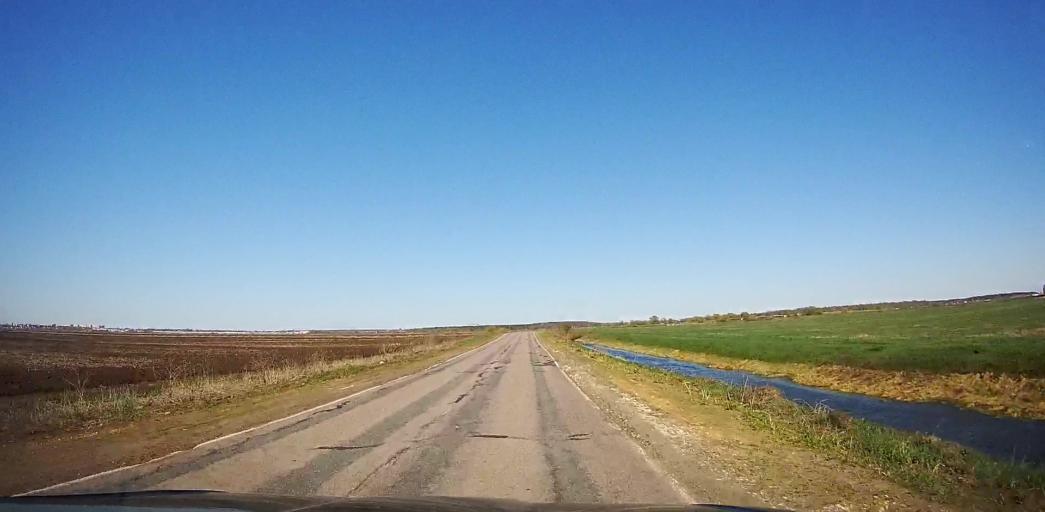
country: RU
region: Moskovskaya
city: Ramenskoye
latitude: 55.5117
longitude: 38.2605
